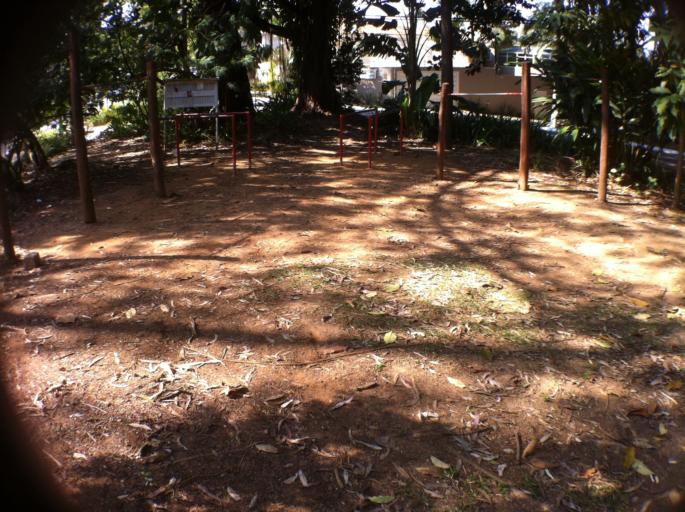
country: BR
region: Sao Paulo
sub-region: Diadema
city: Diadema
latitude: -23.6534
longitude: -46.6863
